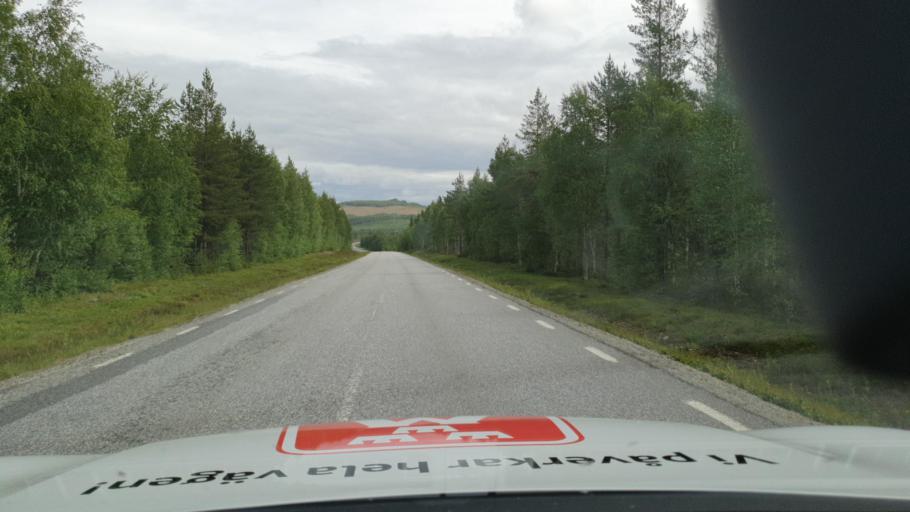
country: SE
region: Vaesterbotten
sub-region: Asele Kommun
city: Asele
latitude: 64.2119
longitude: 16.9186
